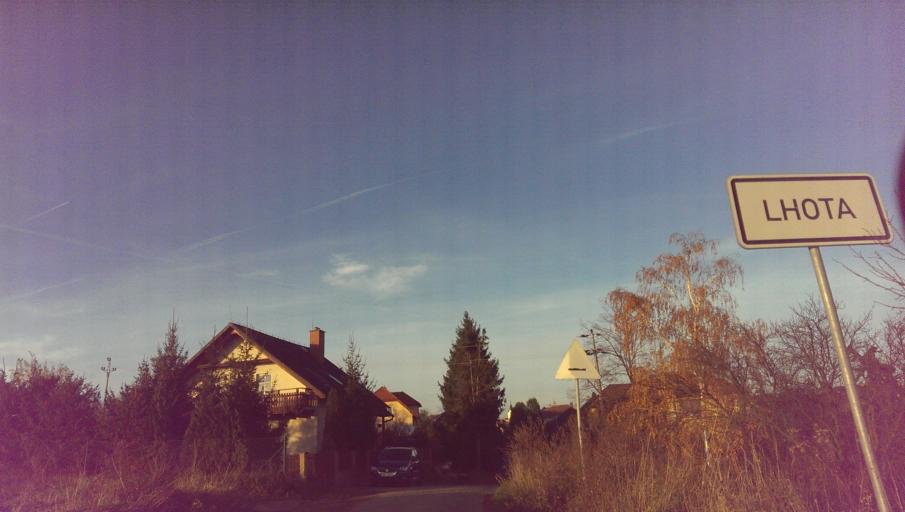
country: CZ
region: Zlin
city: Brezolupy
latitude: 49.1647
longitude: 17.6014
